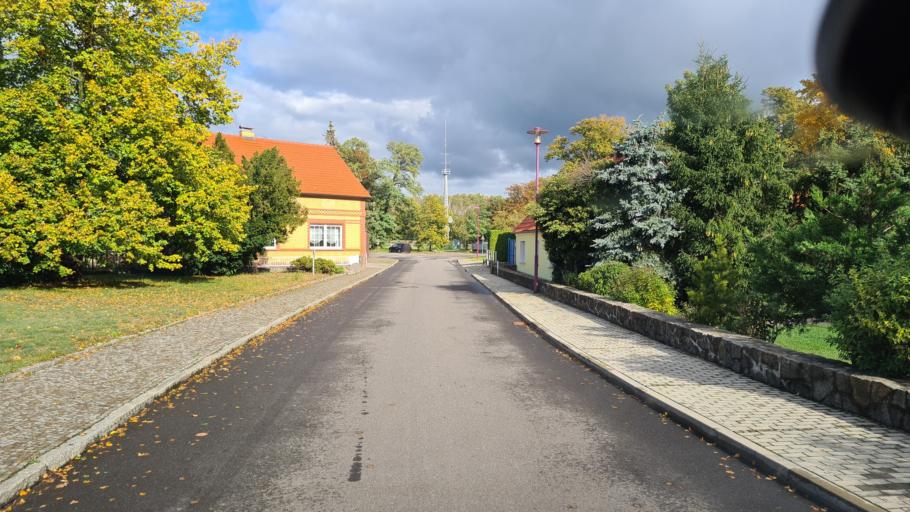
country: DE
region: Brandenburg
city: Grossraschen
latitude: 51.5835
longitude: 13.9618
